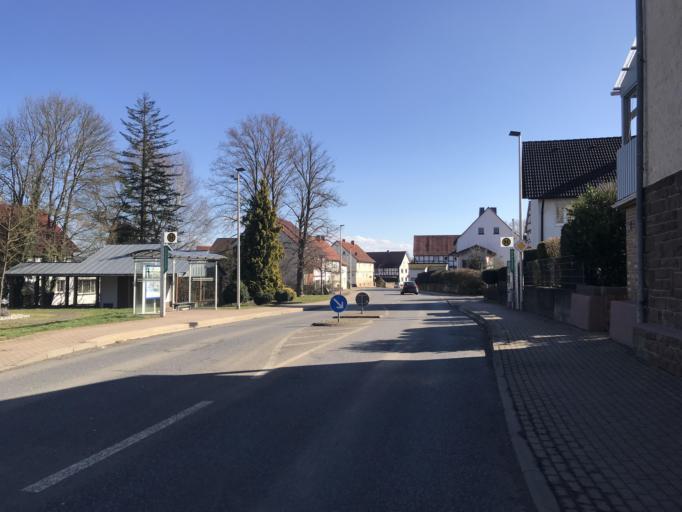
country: DE
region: Hesse
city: Schwalmstadt
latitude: 50.9059
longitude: 9.2101
